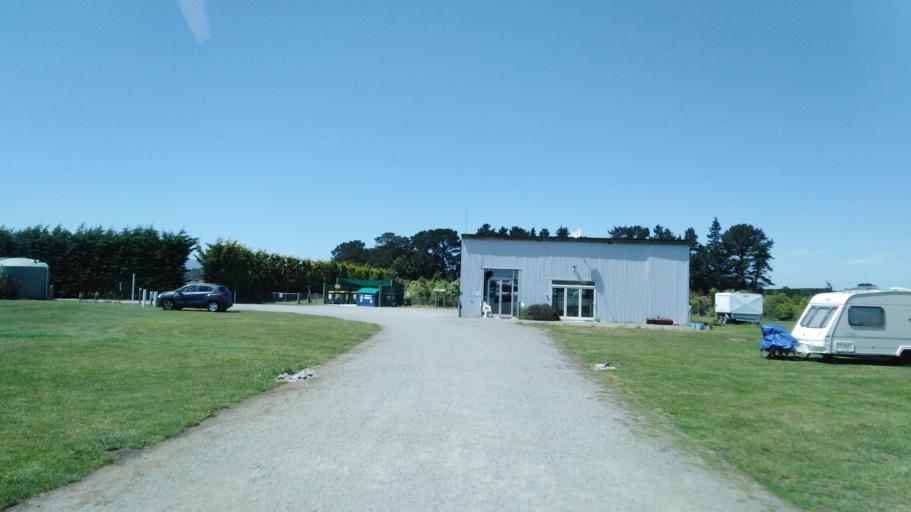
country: NZ
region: Canterbury
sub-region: Selwyn District
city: Rolleston
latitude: -43.5636
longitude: 172.4364
